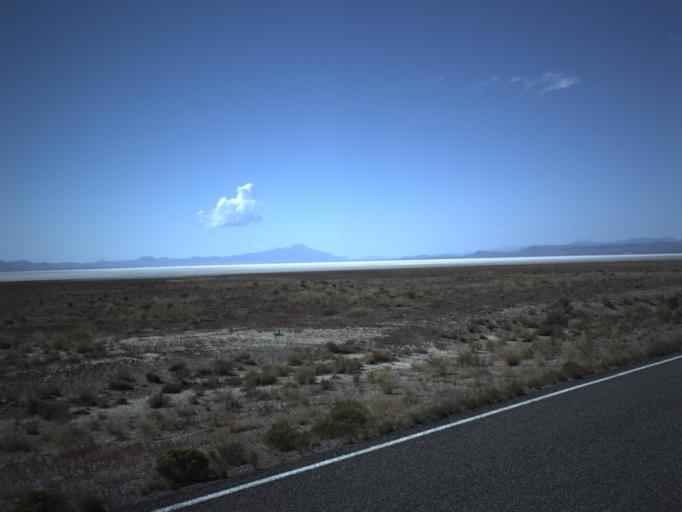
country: US
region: Utah
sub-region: Millard County
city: Delta
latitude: 39.1313
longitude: -113.1018
